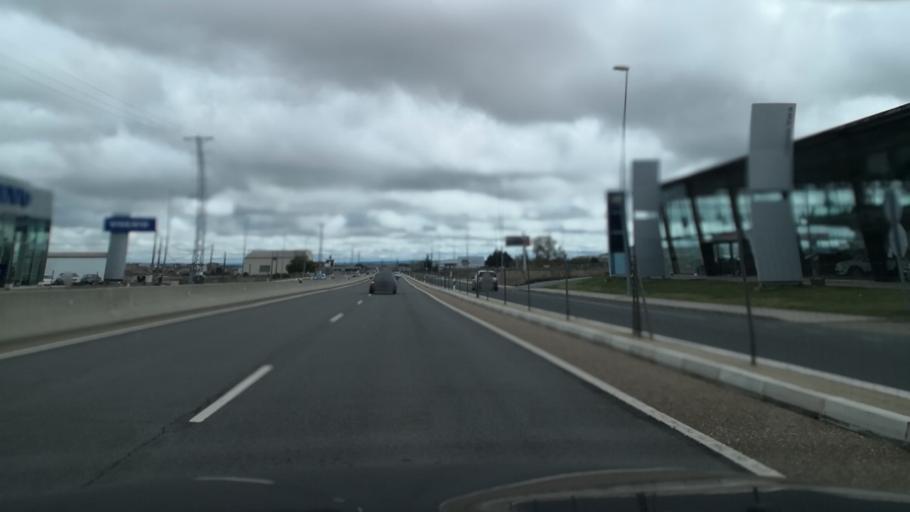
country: ES
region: Castille and Leon
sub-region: Provincia de Zamora
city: Valcabado
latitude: 41.5278
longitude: -5.7585
